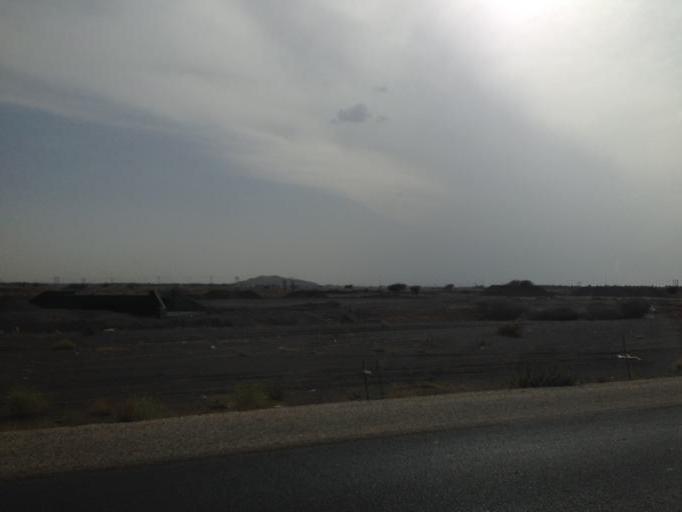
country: OM
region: Ash Sharqiyah
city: Al Qabil
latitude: 22.5584
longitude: 58.7121
